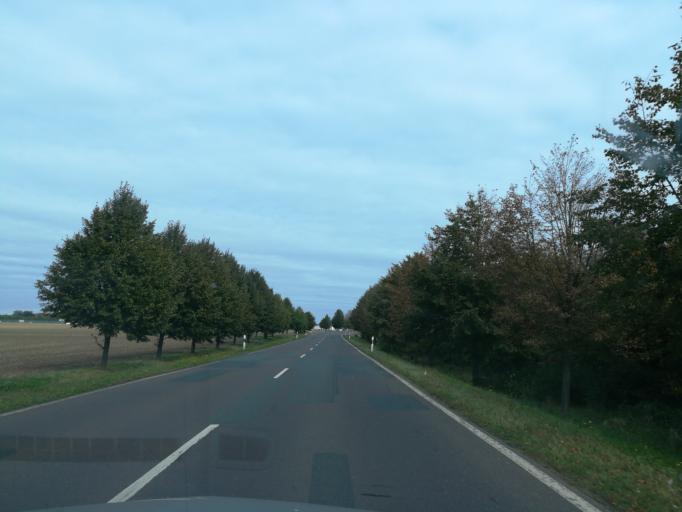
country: DE
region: Saxony-Anhalt
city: Ebendorf
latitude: 52.1804
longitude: 11.5809
